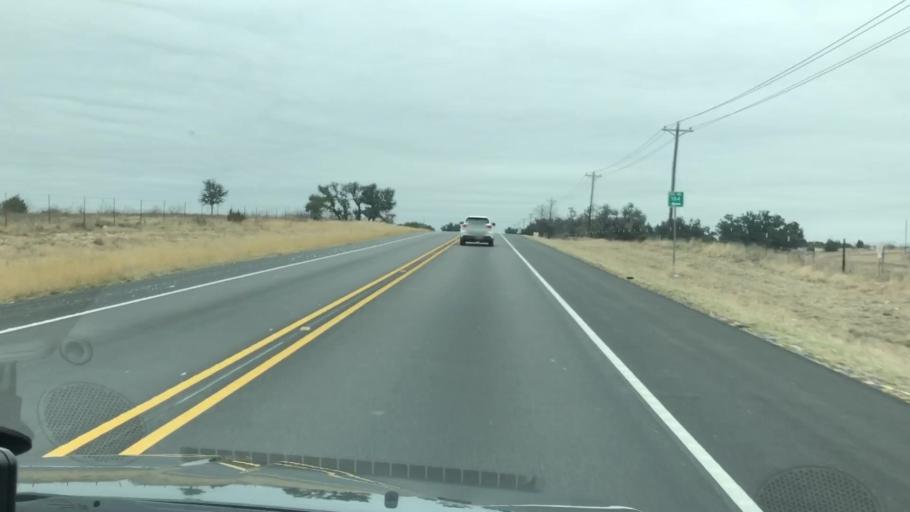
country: US
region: Texas
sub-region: Erath County
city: Stephenville
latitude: 32.3170
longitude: -98.1826
